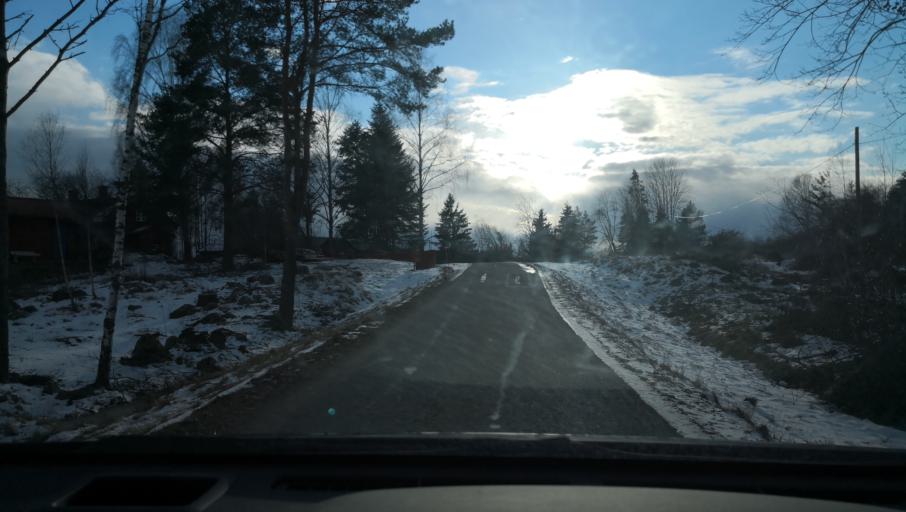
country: SE
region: Uppsala
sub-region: Enkopings Kommun
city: Irsta
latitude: 59.6978
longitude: 16.8641
